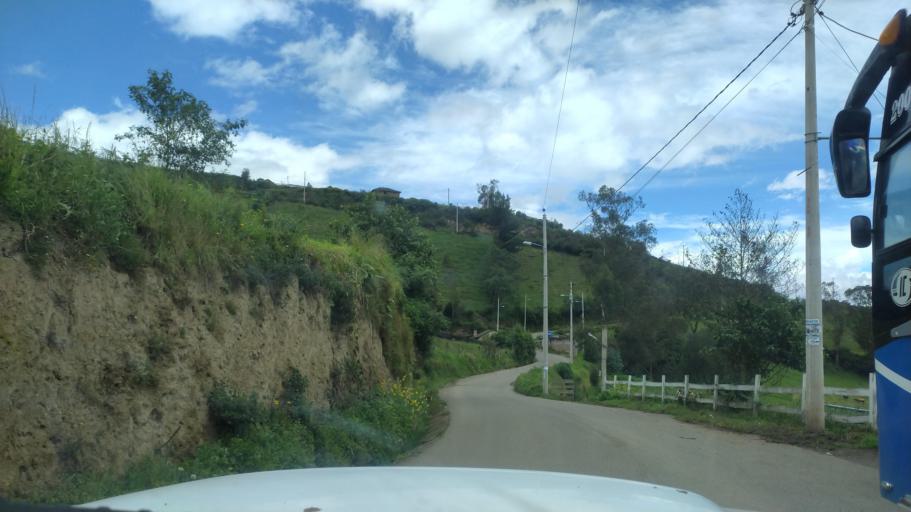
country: EC
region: Chimborazo
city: Riobamba
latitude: -1.6759
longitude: -78.5697
